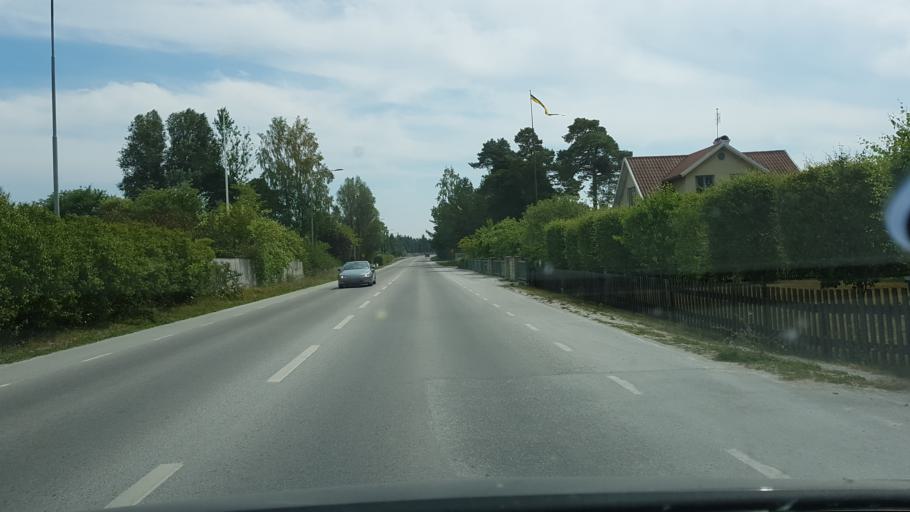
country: SE
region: Gotland
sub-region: Gotland
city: Slite
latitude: 57.7185
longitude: 18.7916
